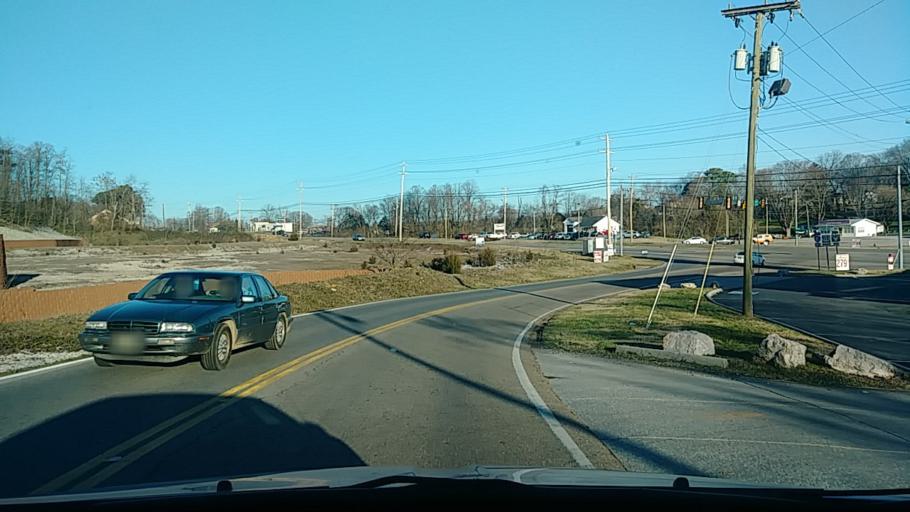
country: US
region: Tennessee
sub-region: Hamblen County
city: Morristown
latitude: 36.1859
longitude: -83.3752
